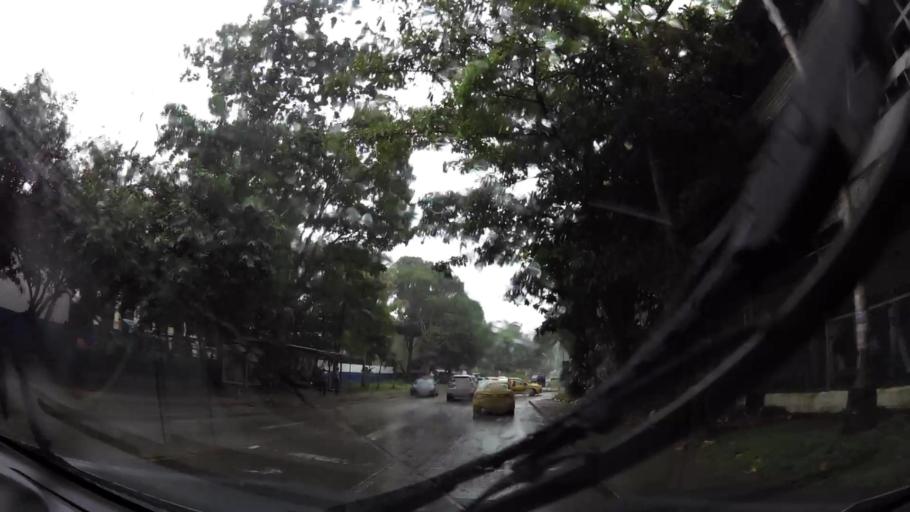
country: PA
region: Panama
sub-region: Distrito de Panama
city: Ancon
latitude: 8.9511
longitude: -79.5543
